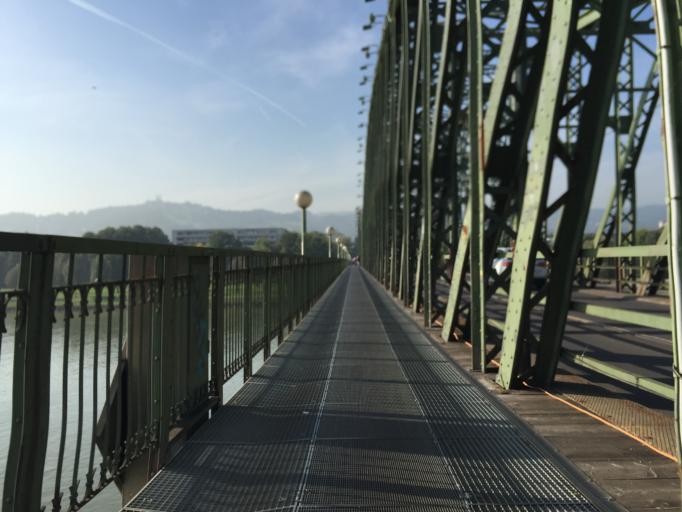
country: AT
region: Upper Austria
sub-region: Linz Stadt
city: Linz
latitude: 48.3168
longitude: 14.2963
